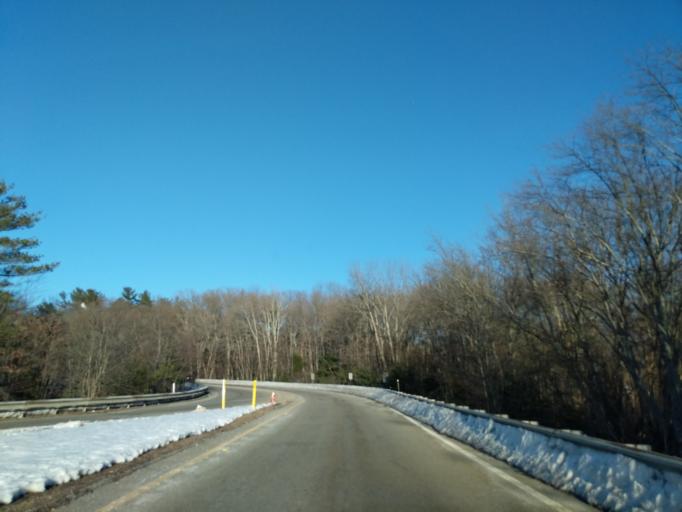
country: US
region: Massachusetts
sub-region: Bristol County
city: Raynham Center
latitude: 41.9031
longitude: -71.0435
